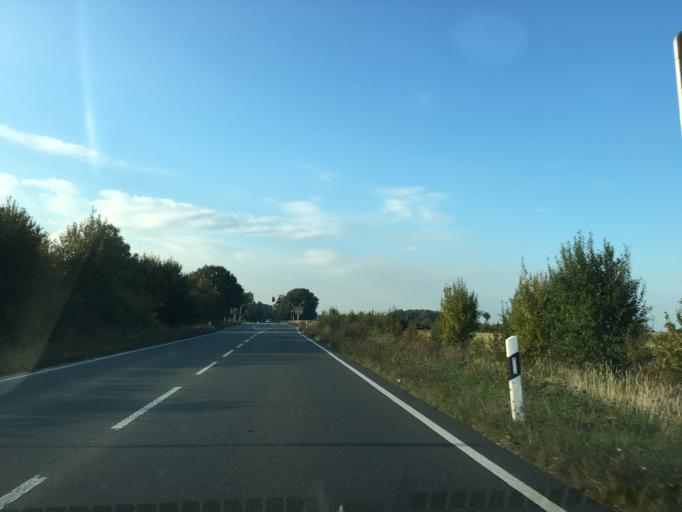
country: DE
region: North Rhine-Westphalia
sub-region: Regierungsbezirk Munster
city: Dulmen
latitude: 51.8260
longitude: 7.3297
